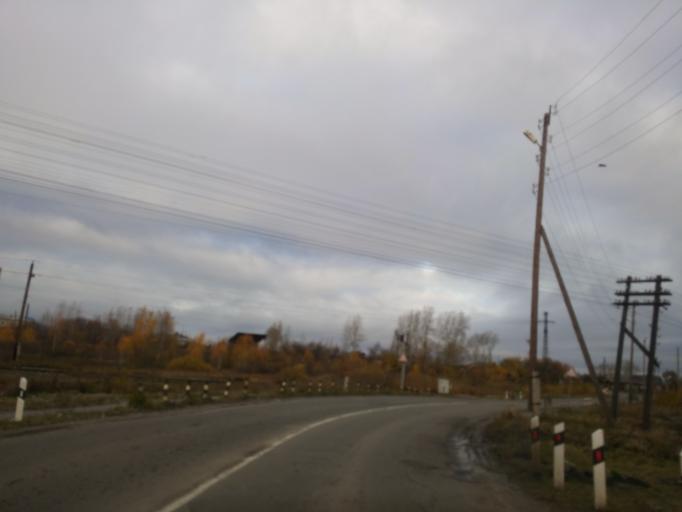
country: RU
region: Sverdlovsk
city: Turinsk
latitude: 58.0302
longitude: 63.7032
